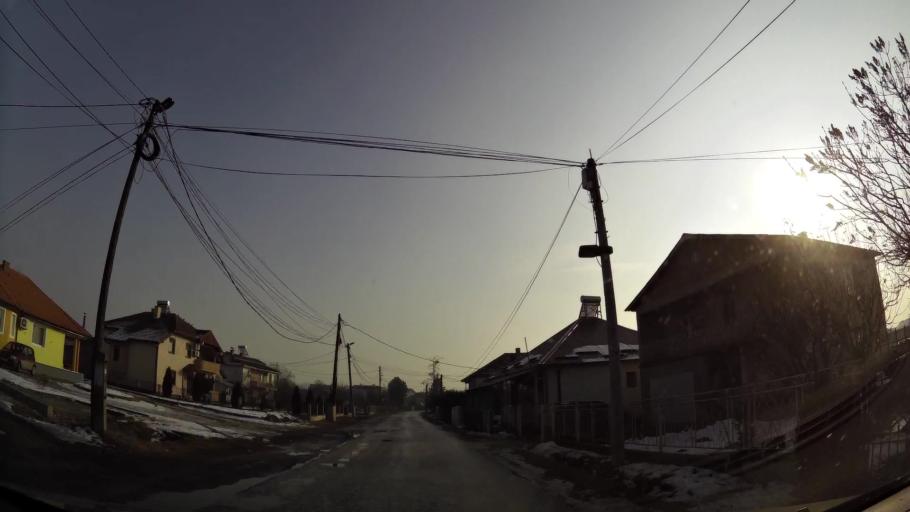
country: MK
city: Kadino
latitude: 41.9592
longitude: 21.6015
